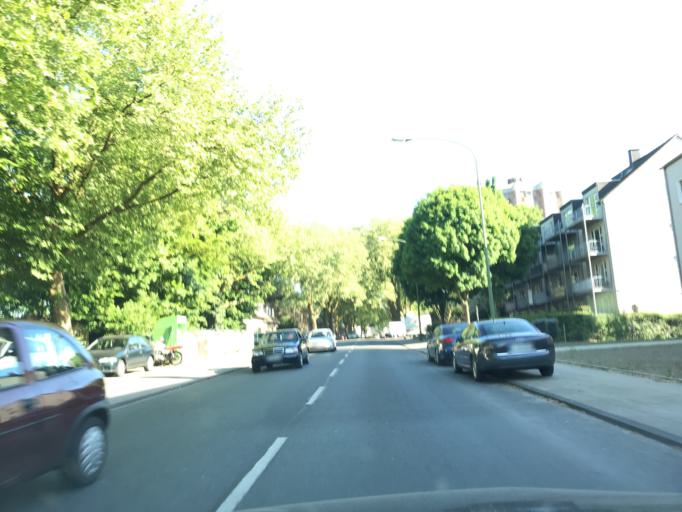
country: DE
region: North Rhine-Westphalia
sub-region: Regierungsbezirk Dusseldorf
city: Essen
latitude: 51.4627
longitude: 7.0469
